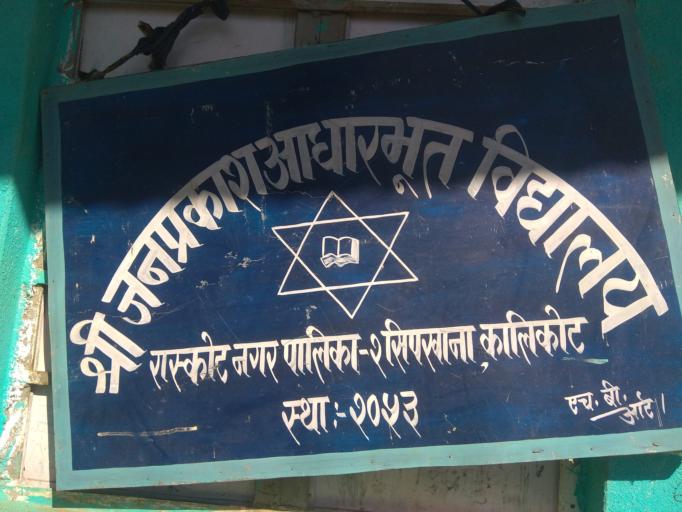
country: NP
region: Far Western
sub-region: Seti Zone
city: Achham
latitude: 29.2538
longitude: 81.6222
